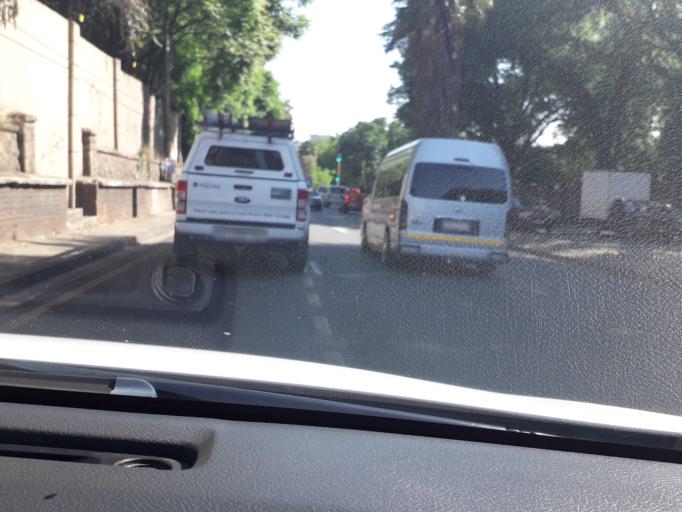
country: ZA
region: Gauteng
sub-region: City of Johannesburg Metropolitan Municipality
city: Johannesburg
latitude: -26.1696
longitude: 28.0332
